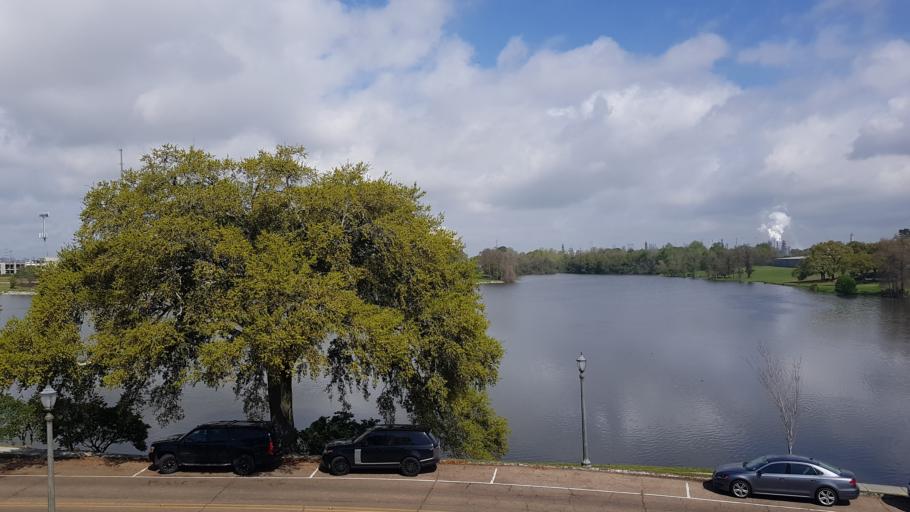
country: US
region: Louisiana
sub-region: West Baton Rouge Parish
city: Port Allen
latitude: 30.4583
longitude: -91.1849
